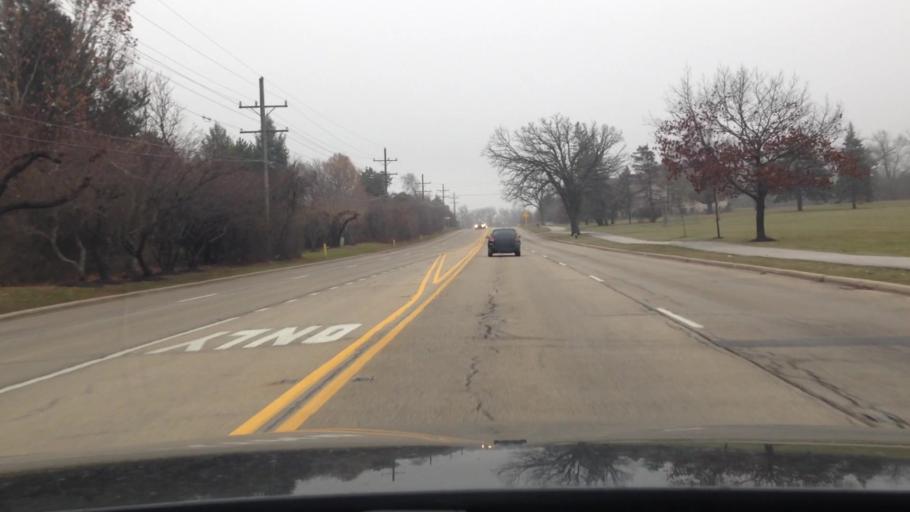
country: US
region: Illinois
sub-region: DuPage County
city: Oakbrook Terrace
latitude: 41.8301
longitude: -87.9718
